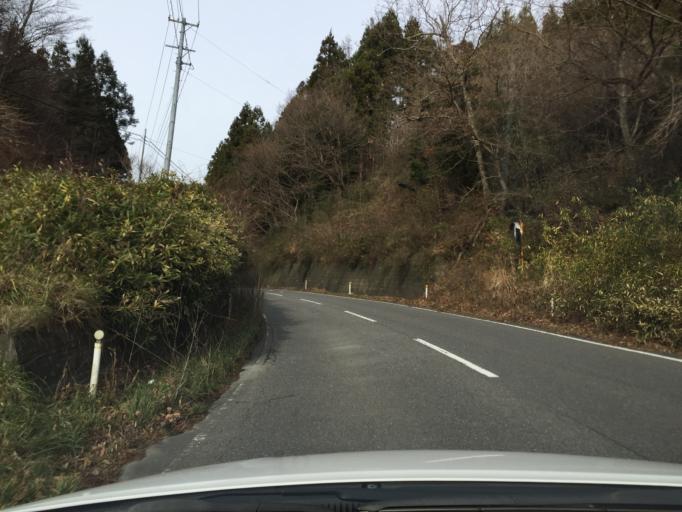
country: JP
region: Fukushima
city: Ishikawa
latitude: 37.2217
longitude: 140.6301
